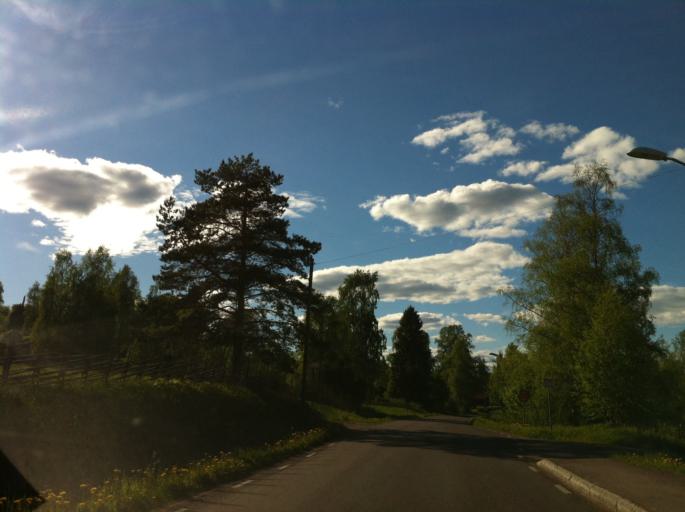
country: SE
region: Dalarna
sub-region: Leksand Municipality
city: Leksand
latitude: 60.7210
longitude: 14.9623
